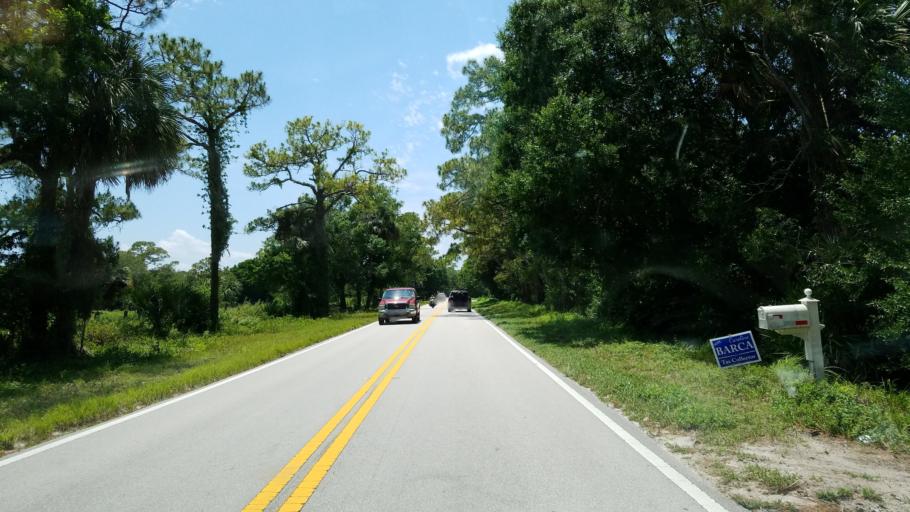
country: US
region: Florida
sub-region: Martin County
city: Indiantown
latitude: 27.1622
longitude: -80.5780
